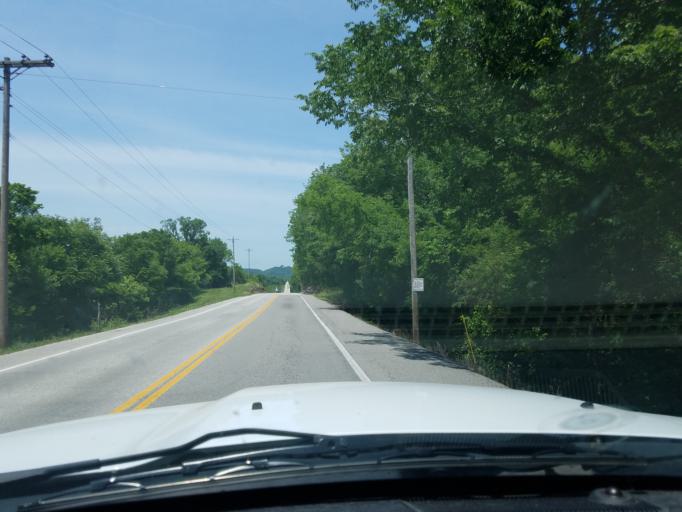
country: US
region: Tennessee
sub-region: Trousdale County
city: Hartsville
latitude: 36.4272
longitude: -86.2663
